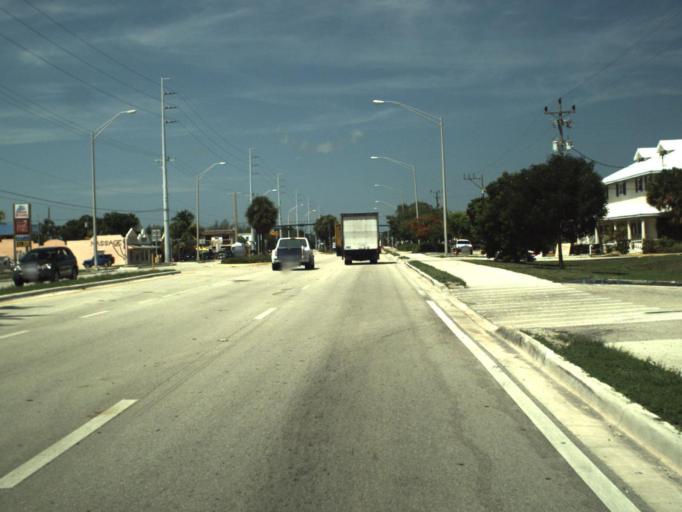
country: US
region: Florida
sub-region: Monroe County
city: Marathon
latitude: 24.7293
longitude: -81.0353
